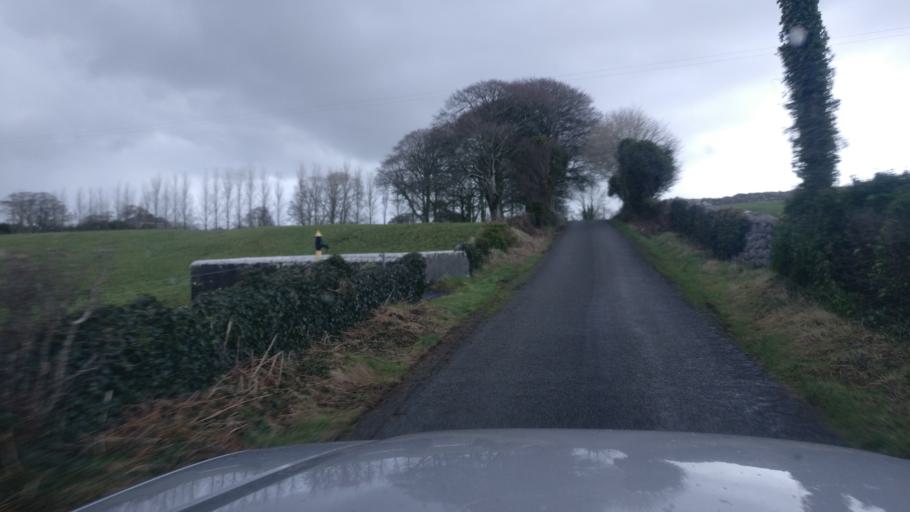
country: IE
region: Connaught
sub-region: County Galway
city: Loughrea
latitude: 53.1837
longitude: -8.6725
